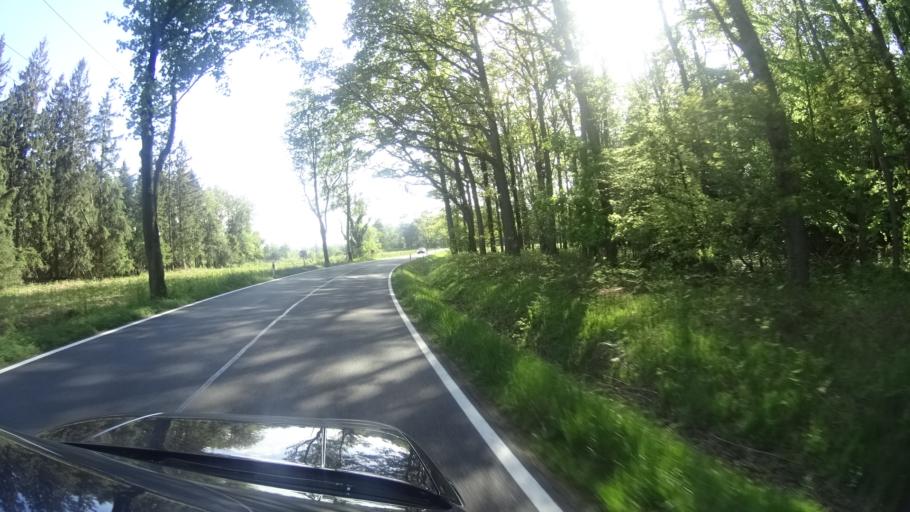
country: DE
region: Mecklenburg-Vorpommern
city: Born
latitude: 54.3978
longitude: 12.5637
